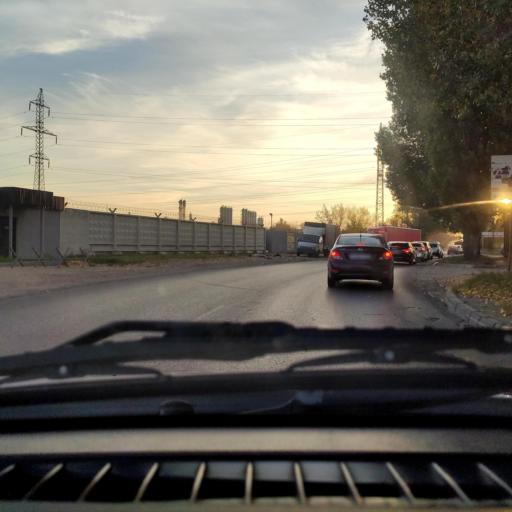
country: RU
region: Samara
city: Tol'yatti
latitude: 53.5356
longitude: 49.4362
